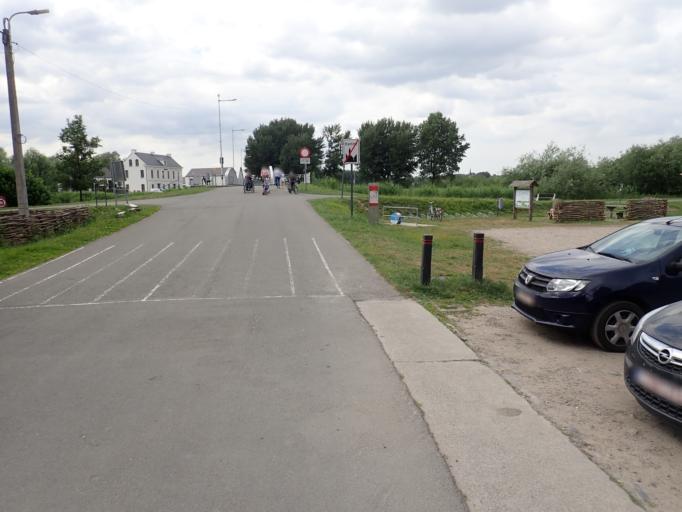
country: BE
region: Flanders
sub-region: Provincie Oost-Vlaanderen
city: Hamme
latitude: 51.1042
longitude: 4.1421
